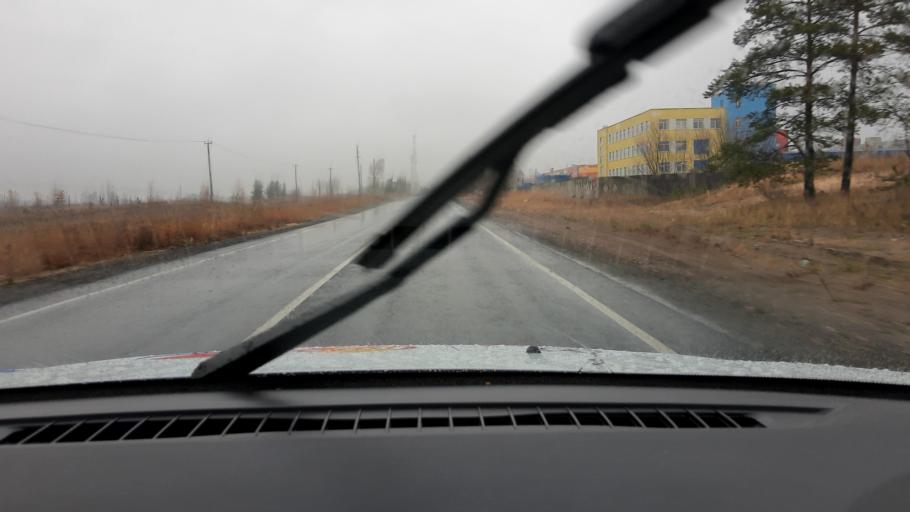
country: RU
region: Nizjnij Novgorod
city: Babino
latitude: 56.2847
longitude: 43.5994
